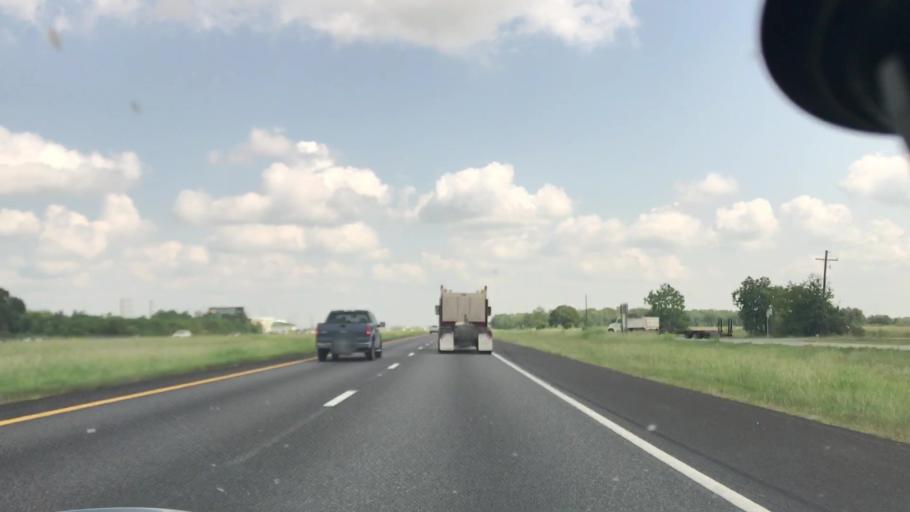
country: US
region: Texas
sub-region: Brazoria County
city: Rosharon
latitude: 29.3987
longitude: -95.4267
